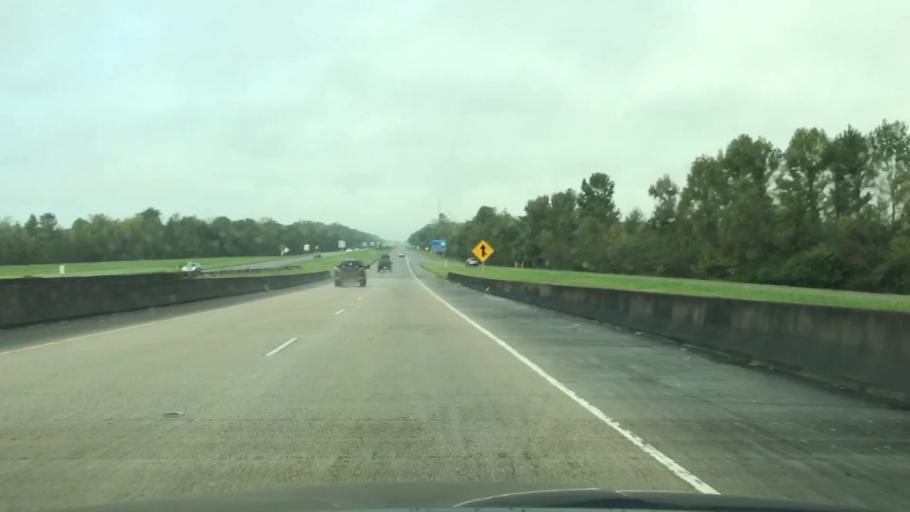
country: US
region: Louisiana
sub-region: Terrebonne Parish
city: Gray
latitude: 29.6825
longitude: -90.7535
